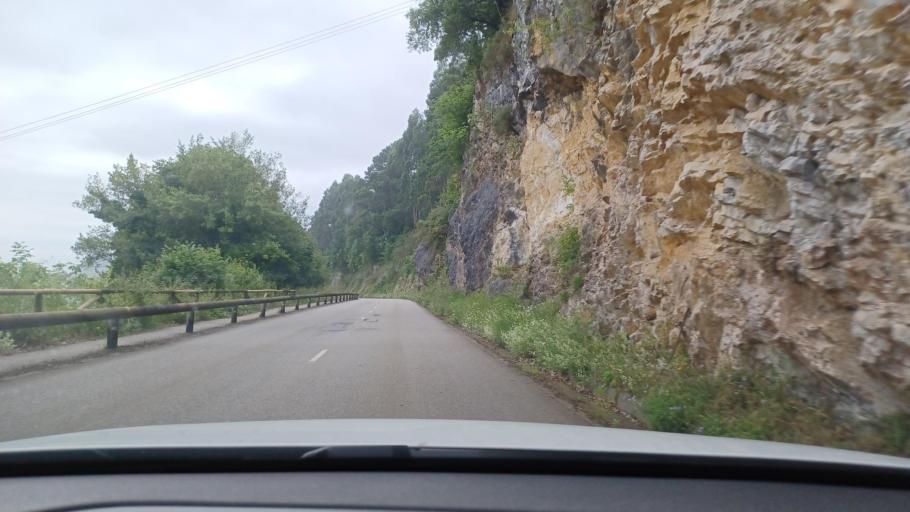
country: ES
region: Asturias
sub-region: Province of Asturias
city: Ribadesella
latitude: 43.4634
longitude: -5.0819
